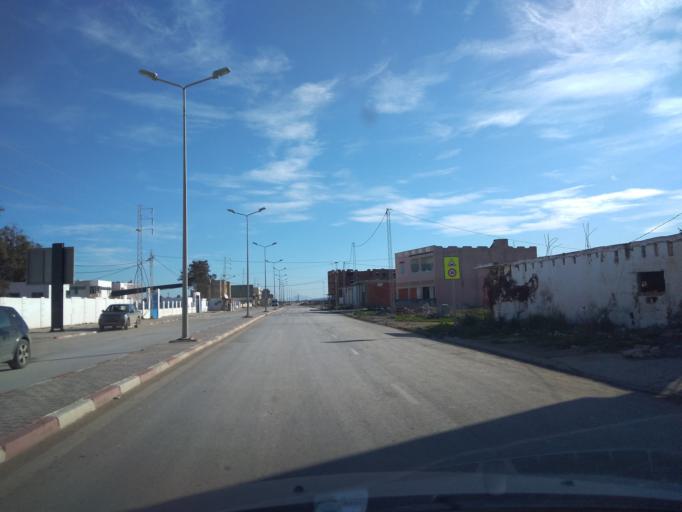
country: TN
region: Ariana
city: Qal'at al Andalus
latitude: 37.0544
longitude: 10.1214
